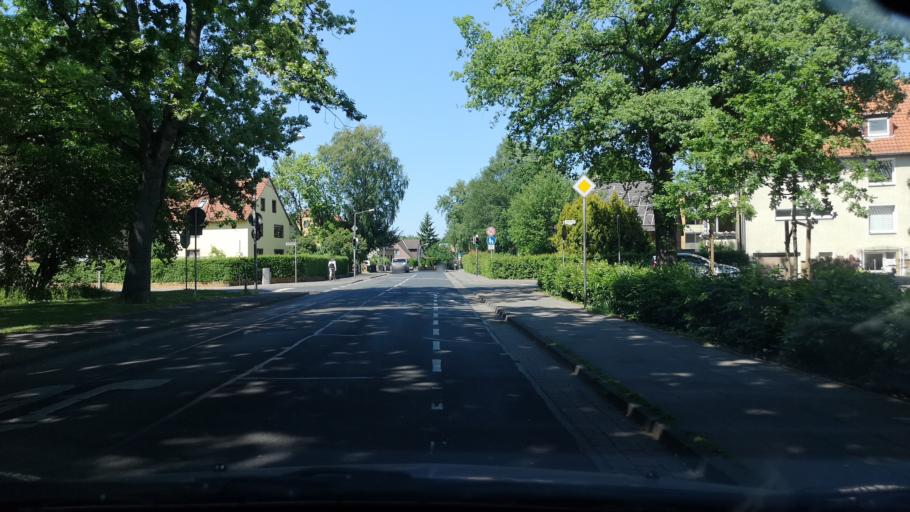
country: DE
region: Lower Saxony
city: Garbsen-Mitte
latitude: 52.4393
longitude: 9.6092
